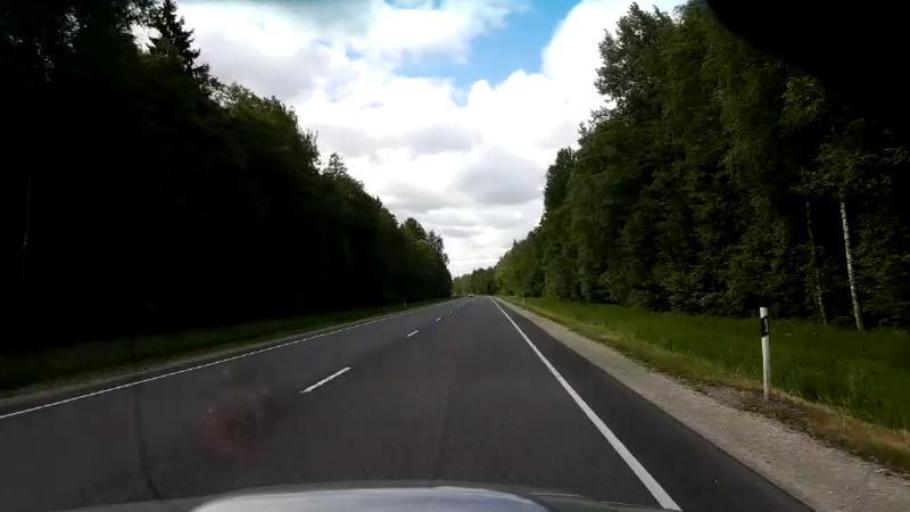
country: EE
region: Raplamaa
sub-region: Maerjamaa vald
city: Marjamaa
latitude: 58.8277
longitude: 24.4161
